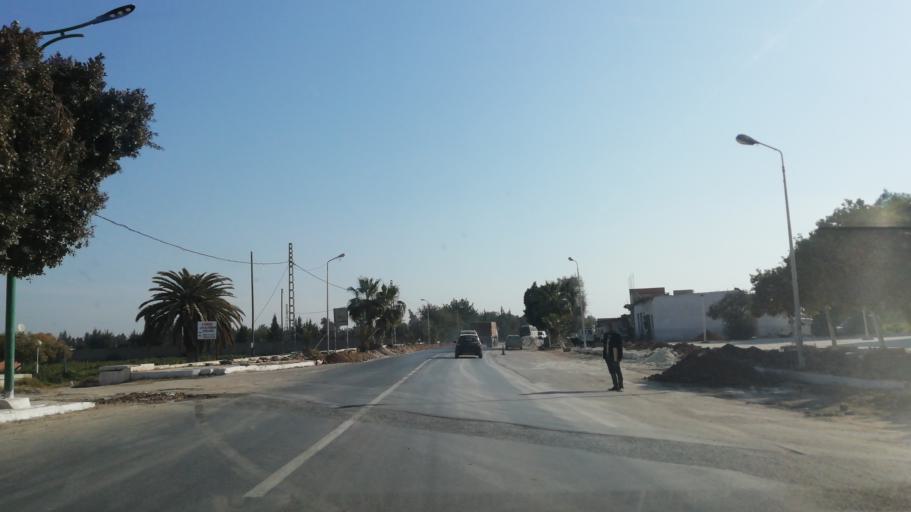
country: DZ
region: Relizane
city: Relizane
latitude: 35.7343
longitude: 0.4658
